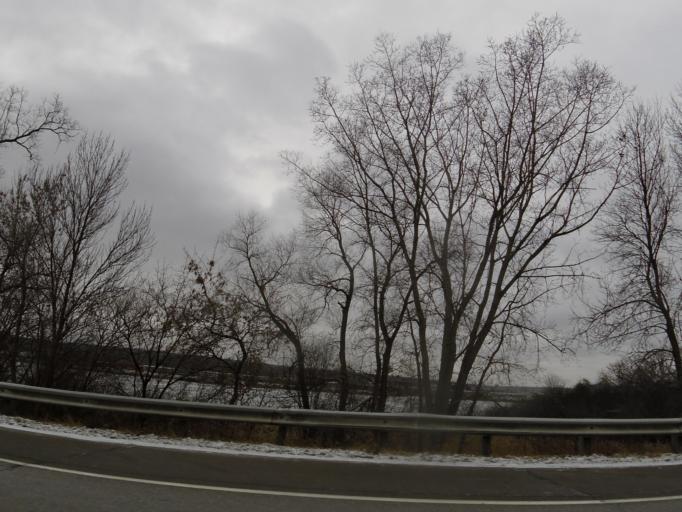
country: US
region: Minnesota
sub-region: Ramsey County
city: Maplewood
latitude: 44.9417
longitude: -93.0341
